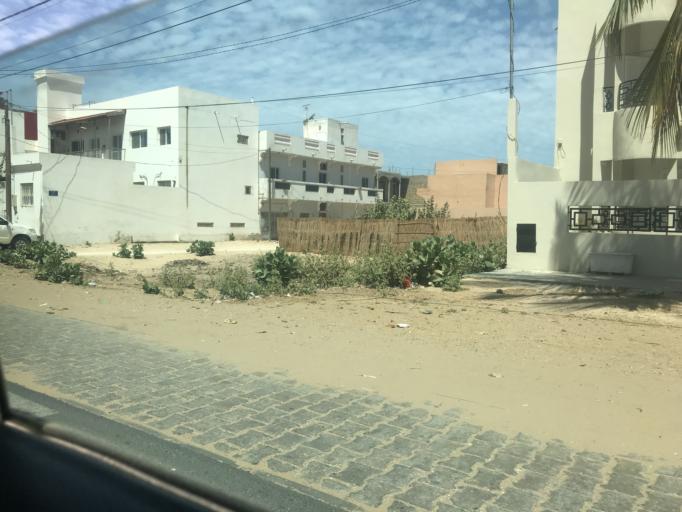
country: SN
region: Saint-Louis
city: Saint-Louis
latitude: 16.0329
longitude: -16.4711
